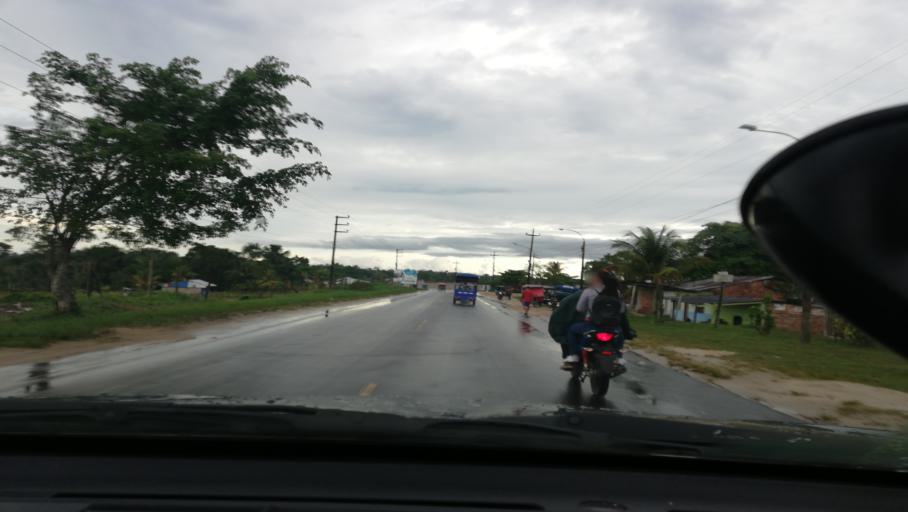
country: PE
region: Loreto
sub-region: Provincia de Maynas
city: Iquitos
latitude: -3.8565
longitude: -73.3379
